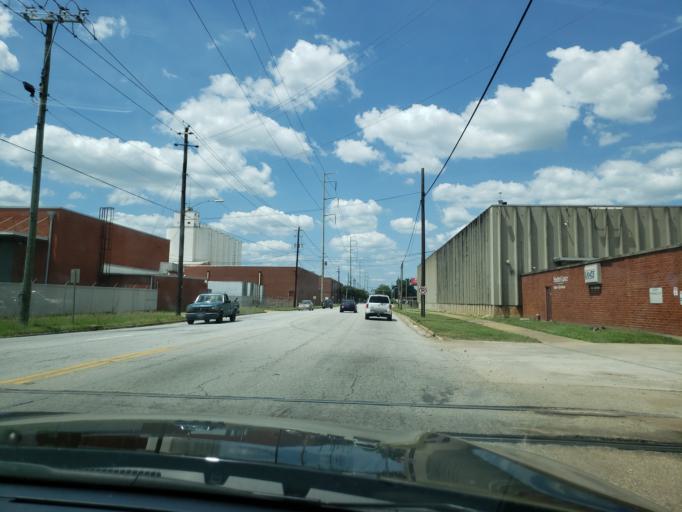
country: US
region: Georgia
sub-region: Muscogee County
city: Columbus
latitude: 32.4554
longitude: -84.9798
